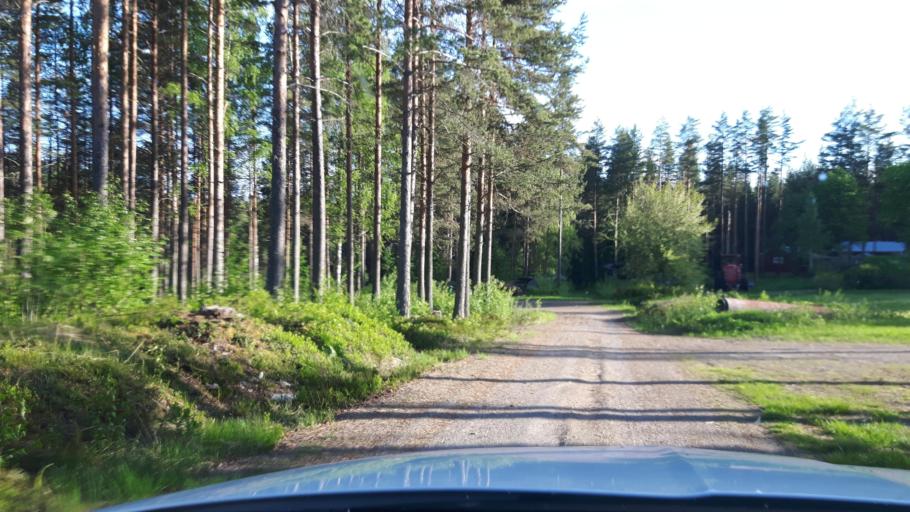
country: SE
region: Gaevleborg
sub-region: Ljusdals Kommun
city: Farila
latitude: 62.0334
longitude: 15.8240
